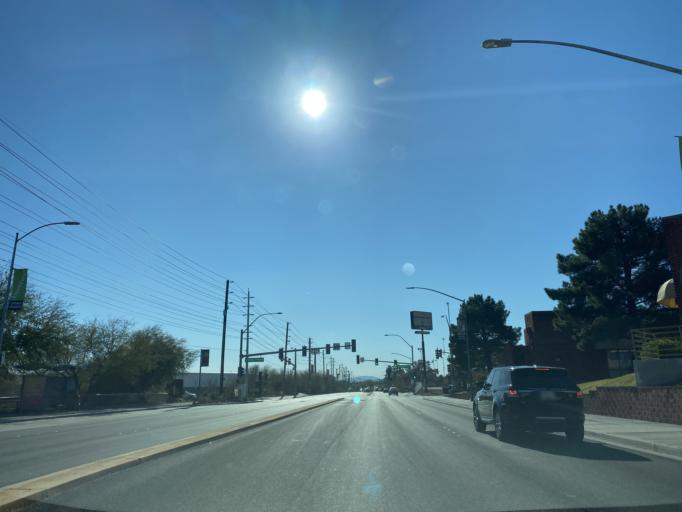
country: US
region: Nevada
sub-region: Clark County
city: Las Vegas
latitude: 36.1709
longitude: -115.1927
